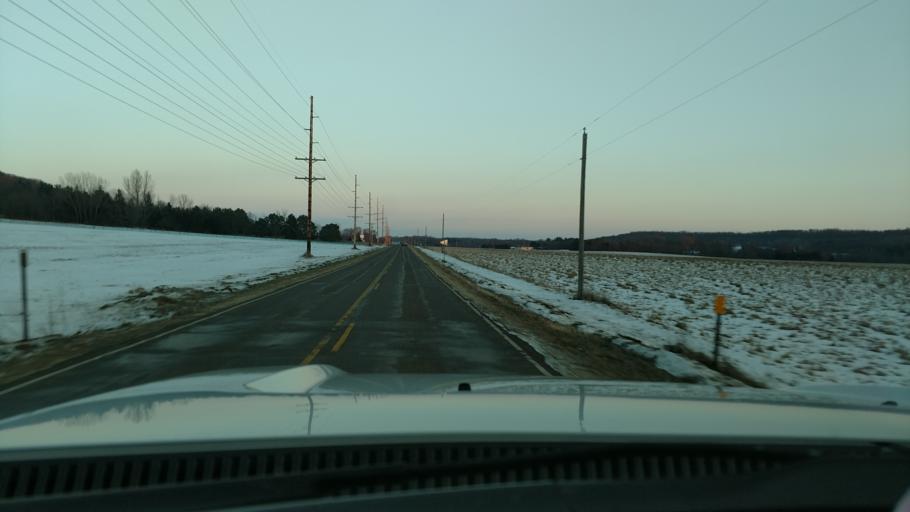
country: US
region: Wisconsin
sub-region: Saint Croix County
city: Roberts
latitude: 44.9129
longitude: -92.5546
